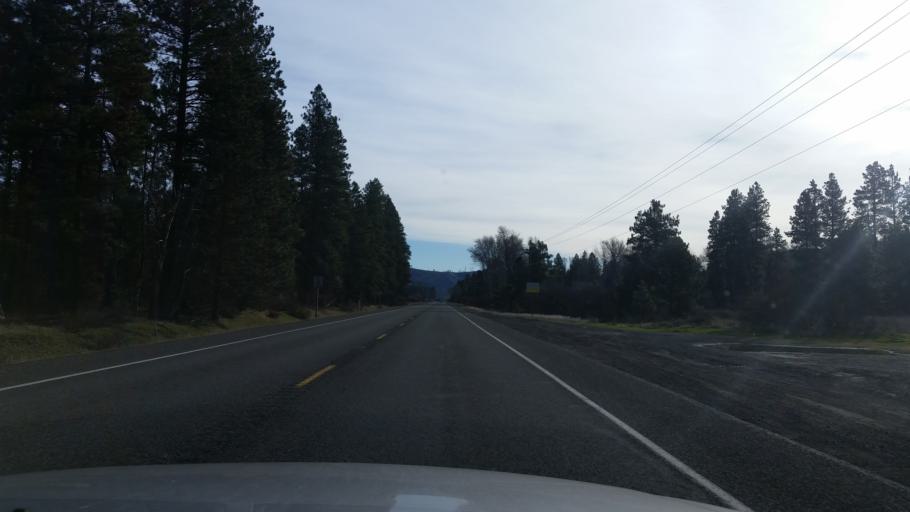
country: US
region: Washington
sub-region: Kittitas County
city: Cle Elum
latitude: 47.1805
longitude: -120.8763
